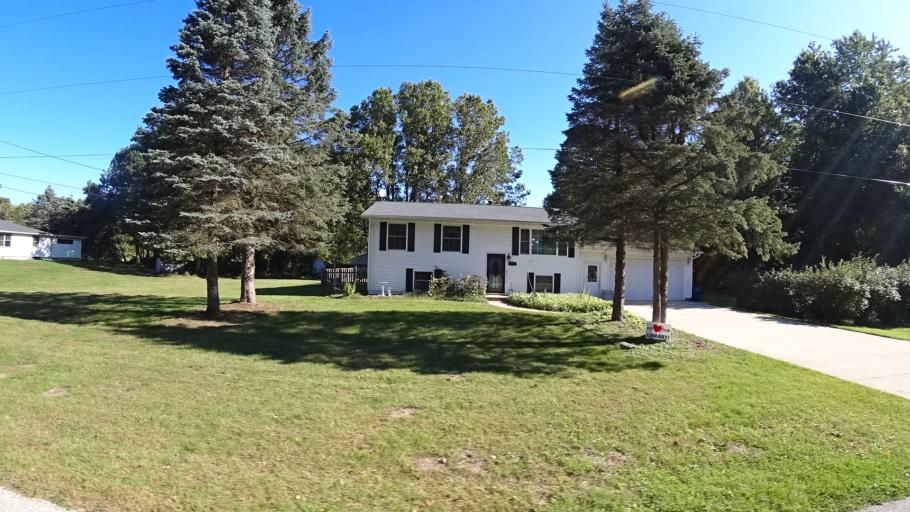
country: US
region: Indiana
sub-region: LaPorte County
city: Michigan City
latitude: 41.6958
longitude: -86.9301
